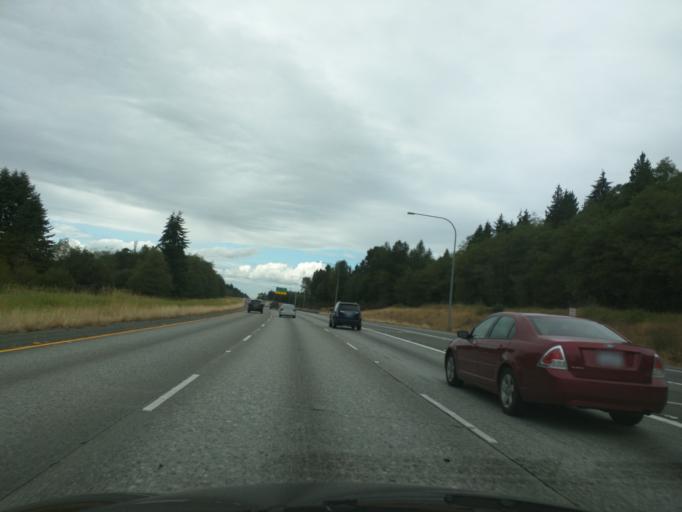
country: US
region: Washington
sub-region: Snohomish County
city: Bryant
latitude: 48.2610
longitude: -122.2606
